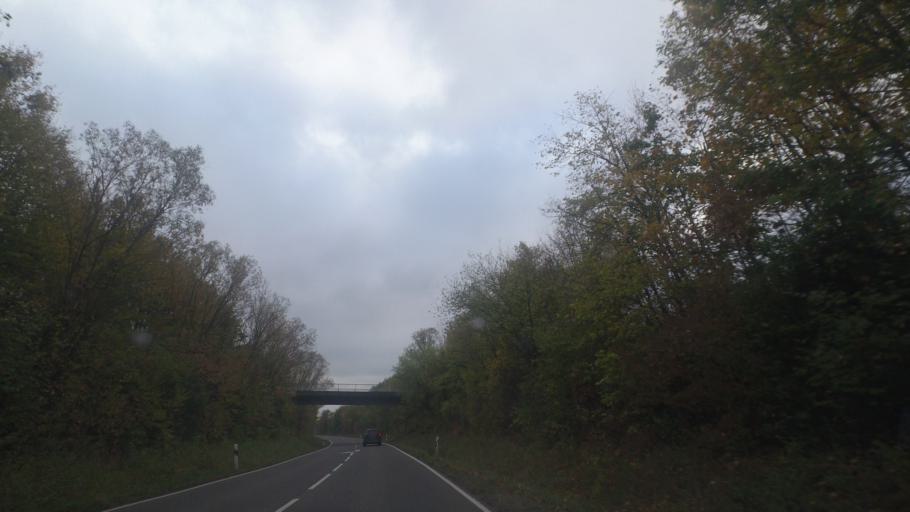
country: DE
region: Rheinland-Pfalz
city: Hillesheim
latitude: 49.7791
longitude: 8.2529
